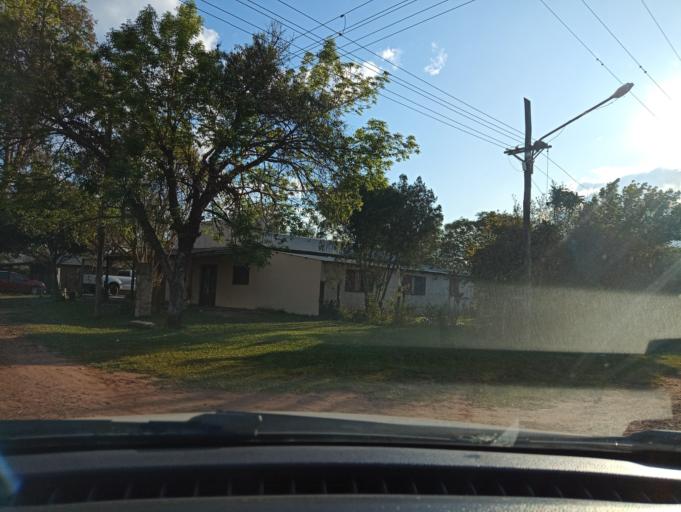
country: AR
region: Corrientes
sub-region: Departamento de San Miguel
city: San Miguel
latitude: -28.5350
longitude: -57.1727
